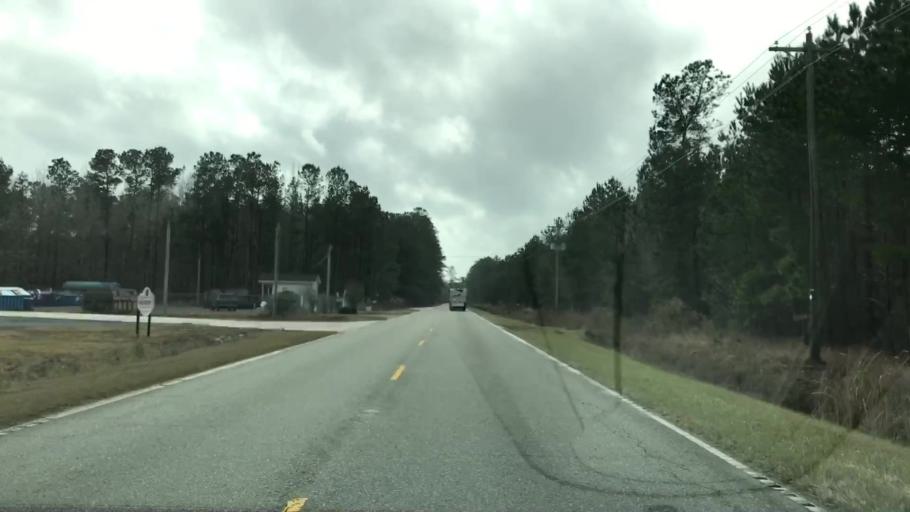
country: US
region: South Carolina
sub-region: Georgetown County
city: Murrells Inlet
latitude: 33.6256
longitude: -79.1908
